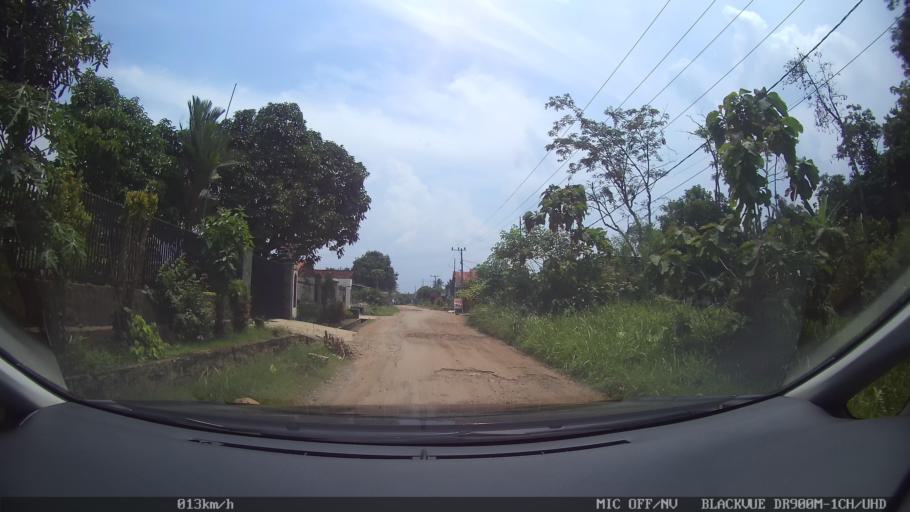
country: ID
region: Lampung
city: Natar
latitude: -5.3130
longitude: 105.2153
